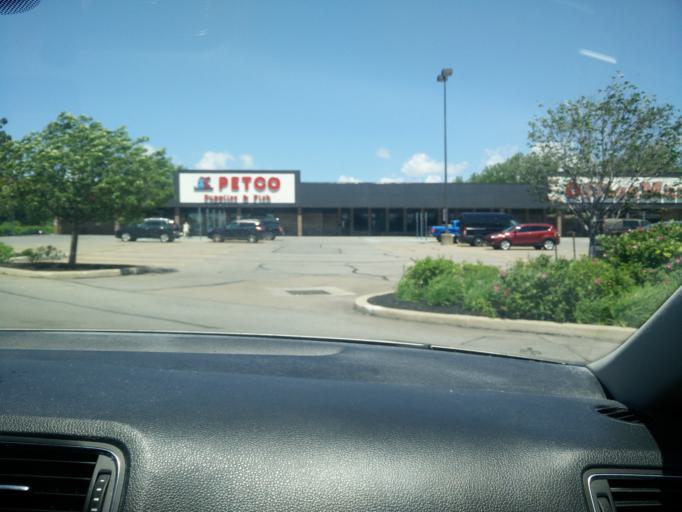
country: US
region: New York
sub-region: Erie County
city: West Seneca
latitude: 42.8356
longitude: -78.7862
